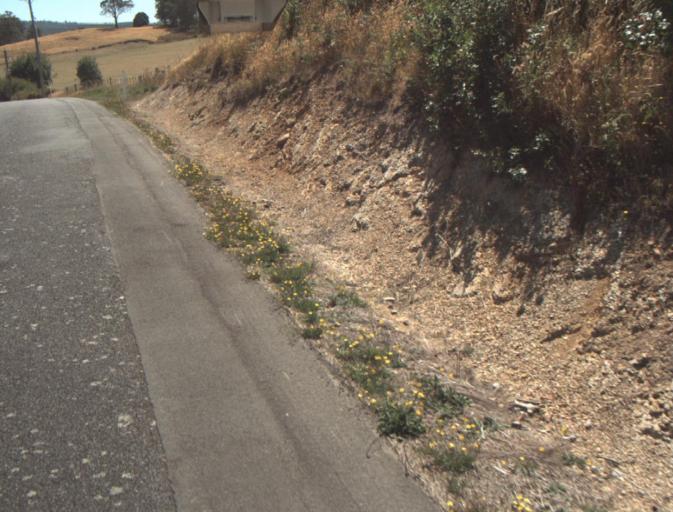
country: AU
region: Tasmania
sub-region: Launceston
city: Newstead
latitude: -41.3454
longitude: 147.3030
